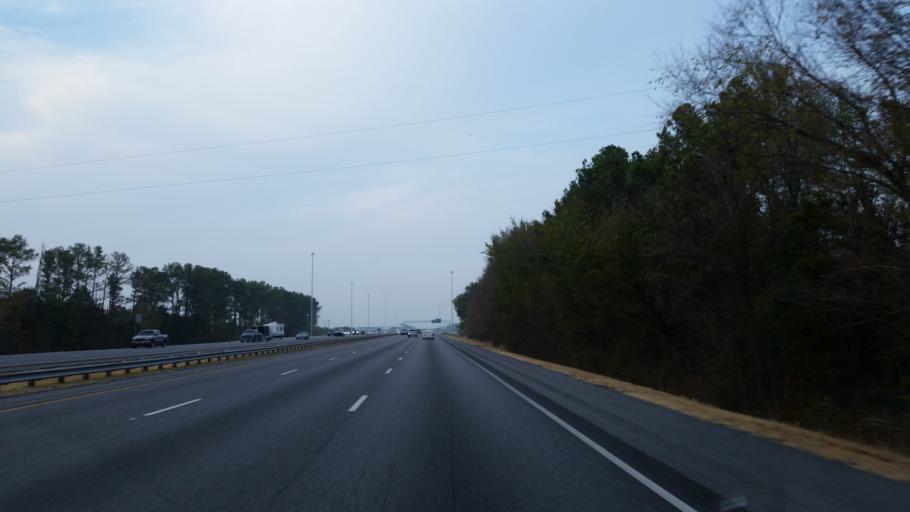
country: US
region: Georgia
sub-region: Bartow County
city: Adairsville
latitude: 34.4312
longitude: -84.9202
